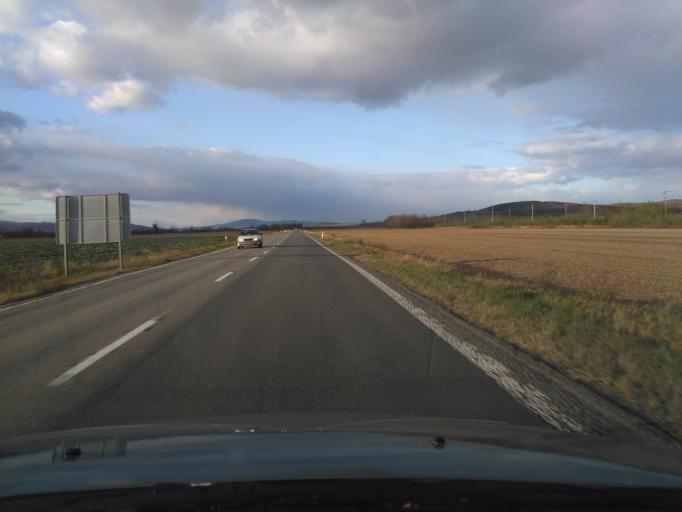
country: HU
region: Borsod-Abauj-Zemplen
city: Satoraljaujhely
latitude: 48.4318
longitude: 21.6584
